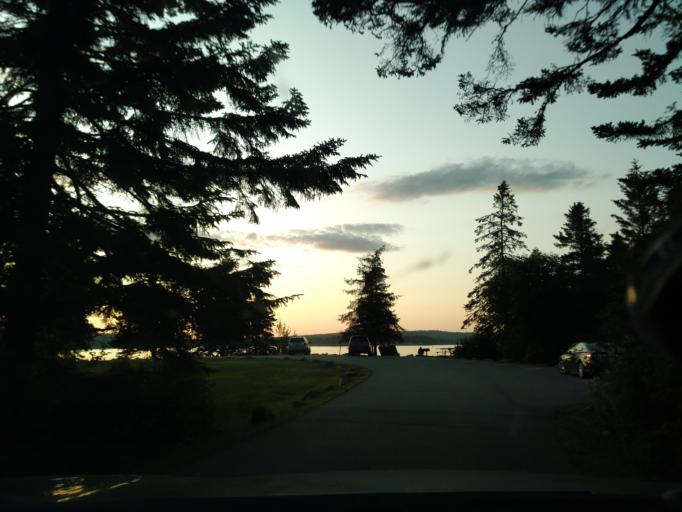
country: US
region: Maine
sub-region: Hancock County
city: Gouldsboro
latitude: 44.3752
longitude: -68.0749
